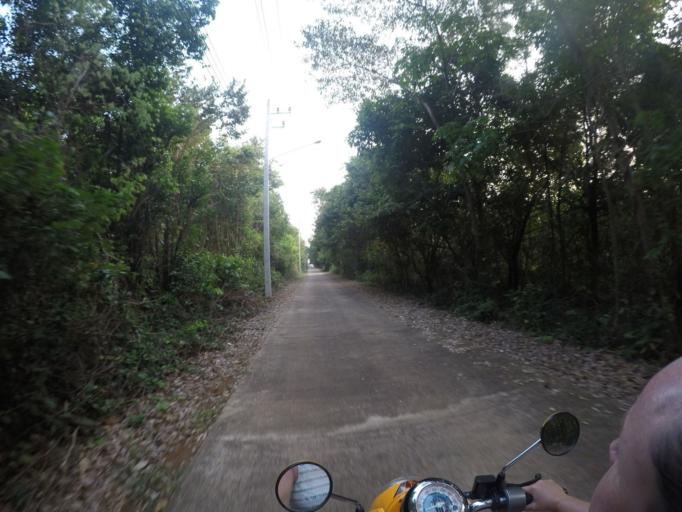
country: TH
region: Trat
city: Ko Kut
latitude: 11.7972
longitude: 102.4871
